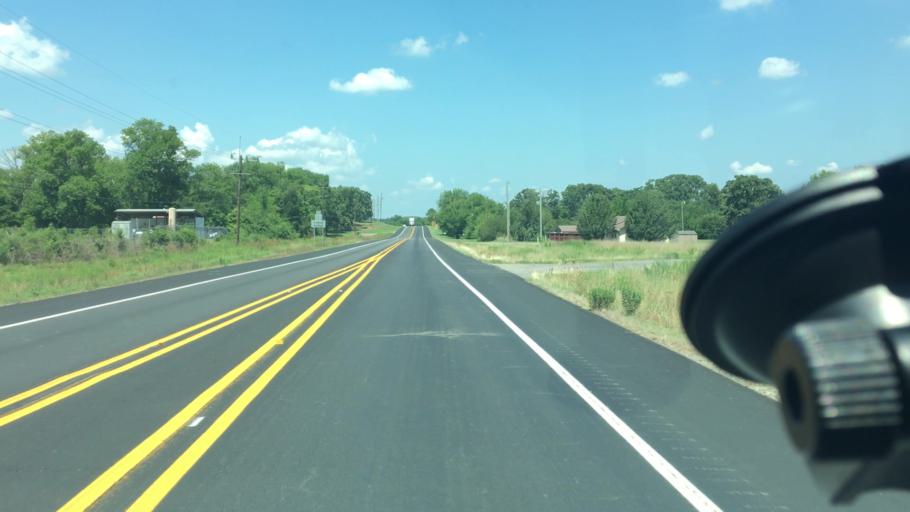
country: US
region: Arkansas
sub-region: Sebastian County
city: Lavaca
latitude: 35.3024
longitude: -94.1637
